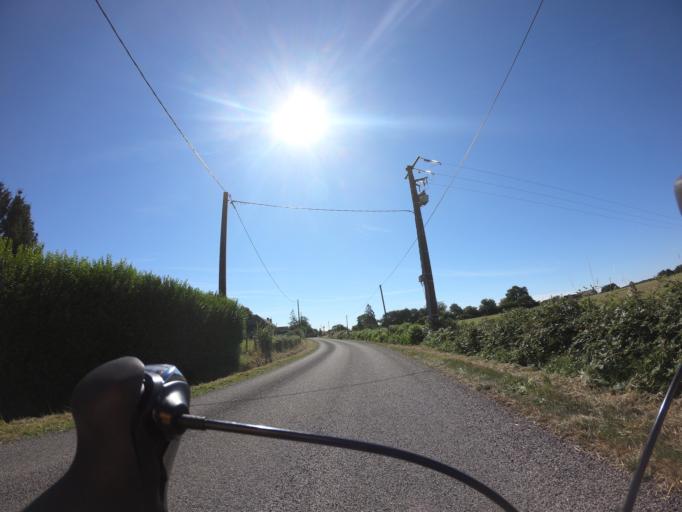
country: FR
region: Lower Normandy
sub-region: Departement de l'Orne
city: Saint-Denis-sur-Sarthon
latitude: 48.5540
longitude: -0.1156
